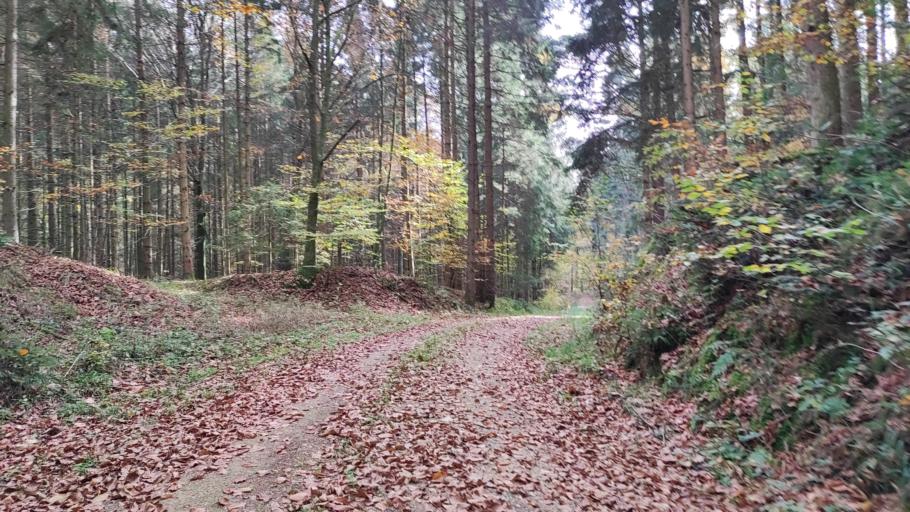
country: DE
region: Bavaria
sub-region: Swabia
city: Langenneufnach
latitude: 48.2781
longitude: 10.5928
